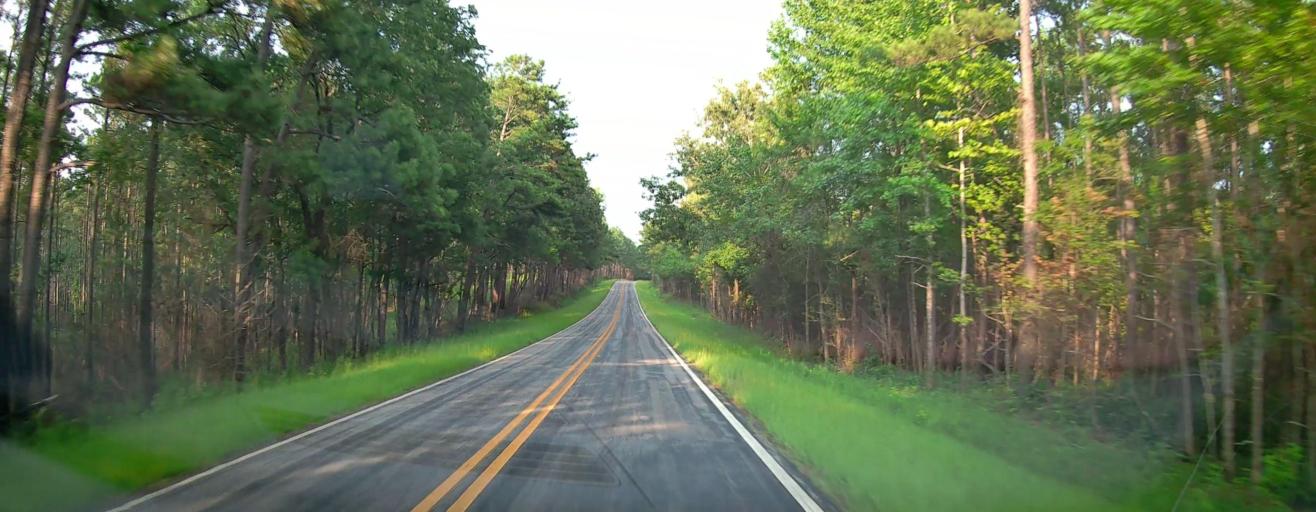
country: US
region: Georgia
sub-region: Jones County
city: Gray
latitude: 33.1166
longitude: -83.6324
